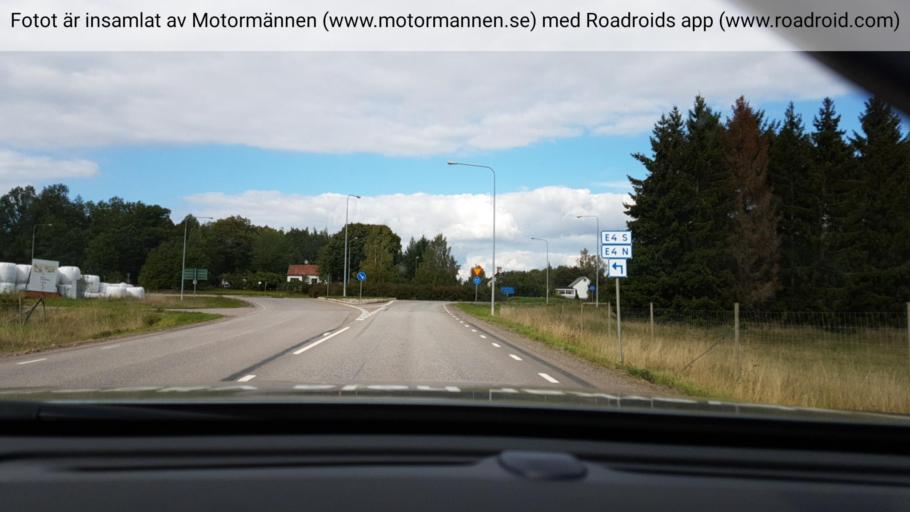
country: SE
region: OEstergoetland
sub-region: Vadstena Kommun
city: Herrestad
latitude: 58.3025
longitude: 14.9209
